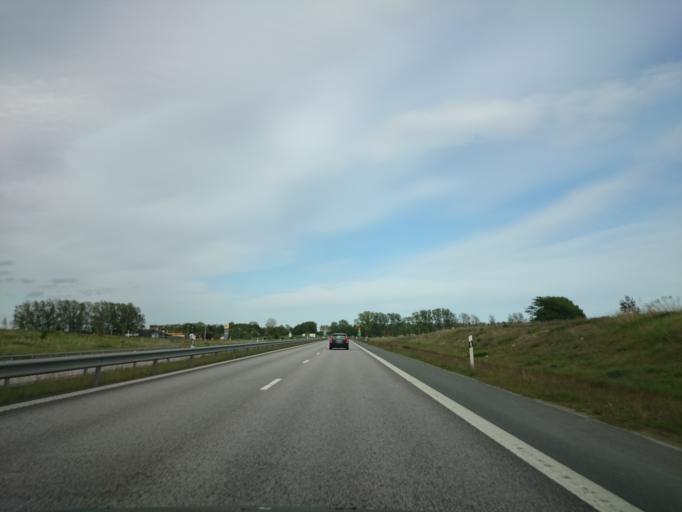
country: SE
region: Skane
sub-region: Kristianstads Kommun
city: Fjalkinge
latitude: 56.0340
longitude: 14.2647
